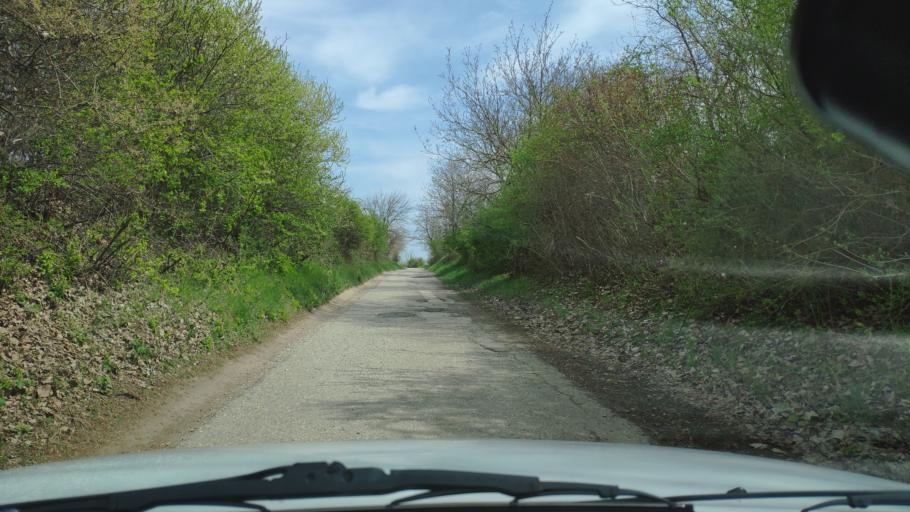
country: HU
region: Zala
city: Nagykanizsa
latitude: 46.4181
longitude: 17.0006
